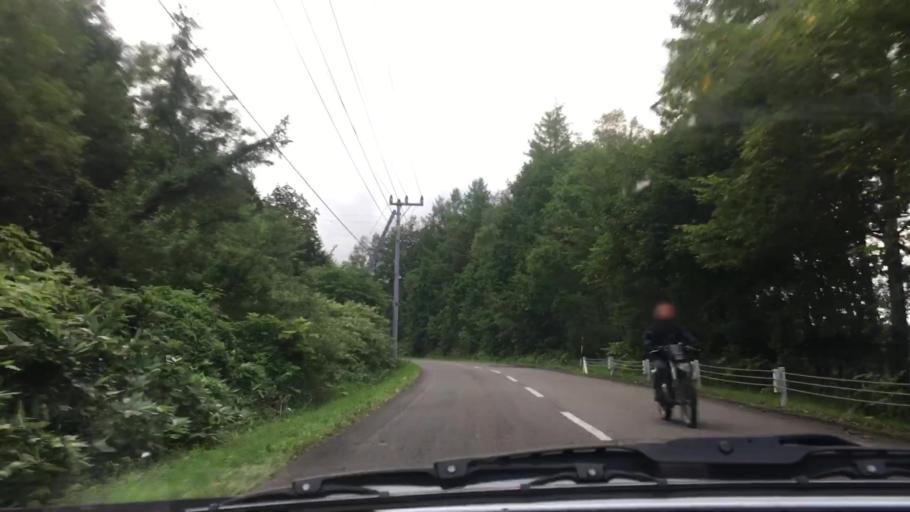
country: JP
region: Hokkaido
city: Otofuke
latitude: 43.1470
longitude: 142.8724
